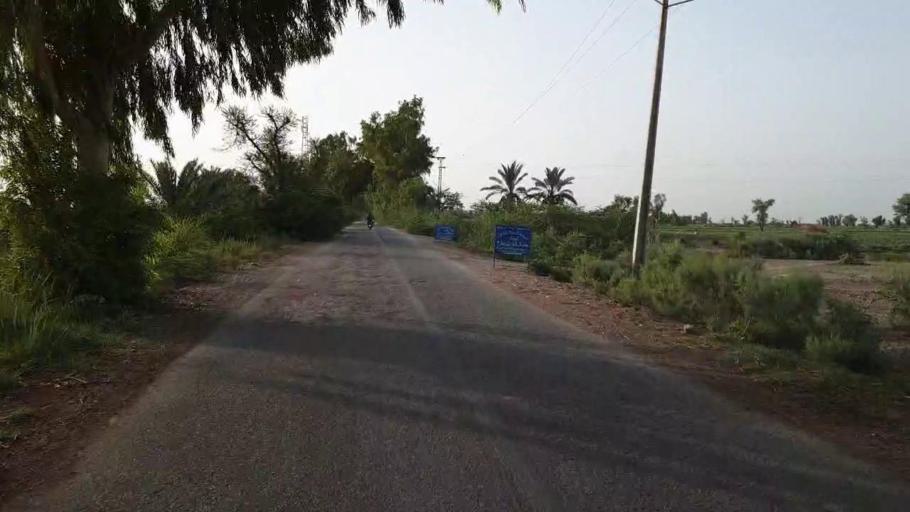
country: PK
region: Sindh
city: Bozdar
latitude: 27.1127
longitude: 68.9588
